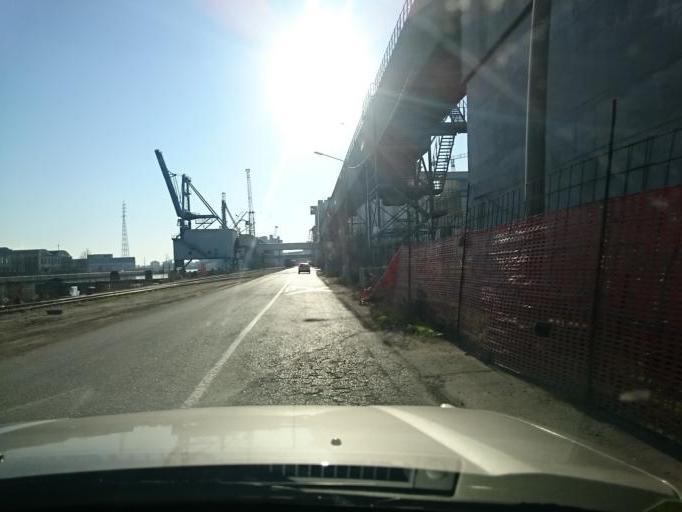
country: IT
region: Veneto
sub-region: Provincia di Venezia
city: Mestre
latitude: 45.4704
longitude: 12.2353
